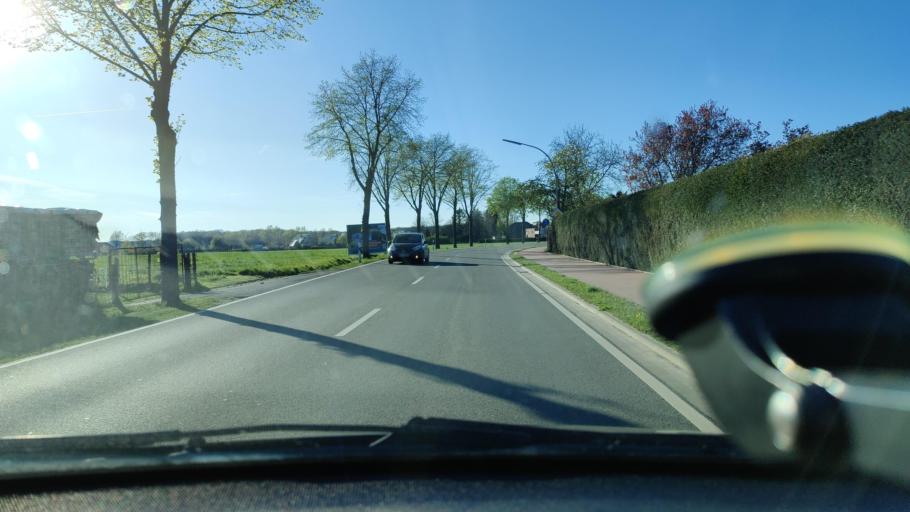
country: DE
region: North Rhine-Westphalia
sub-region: Regierungsbezirk Munster
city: Legden
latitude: 52.0285
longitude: 7.1021
